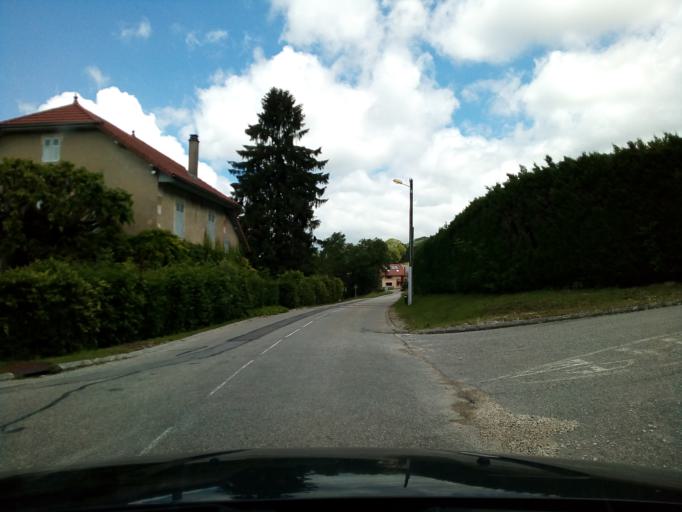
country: FR
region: Rhone-Alpes
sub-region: Departement de la Savoie
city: Saint-Beron
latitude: 45.4824
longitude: 5.7659
